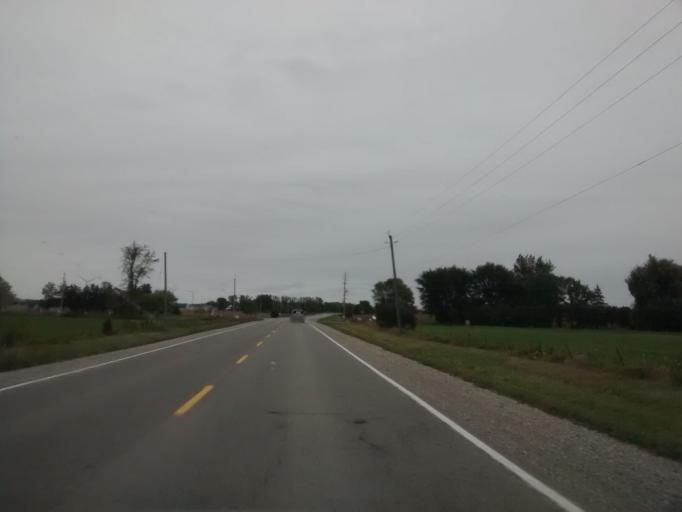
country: CA
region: Ontario
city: Hamilton
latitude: 42.8772
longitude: -79.7074
